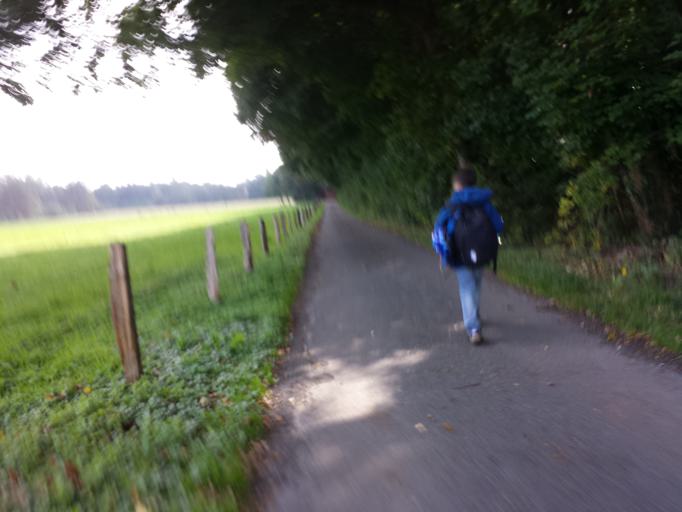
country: DE
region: North Rhine-Westphalia
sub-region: Regierungsbezirk Detmold
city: Langenberg
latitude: 51.7841
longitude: 8.3187
